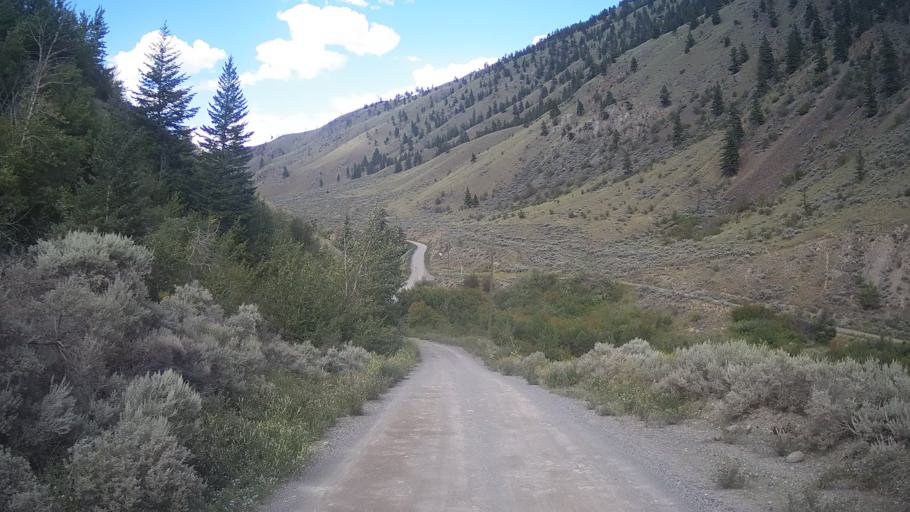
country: CA
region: British Columbia
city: Lillooet
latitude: 51.1999
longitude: -122.1015
